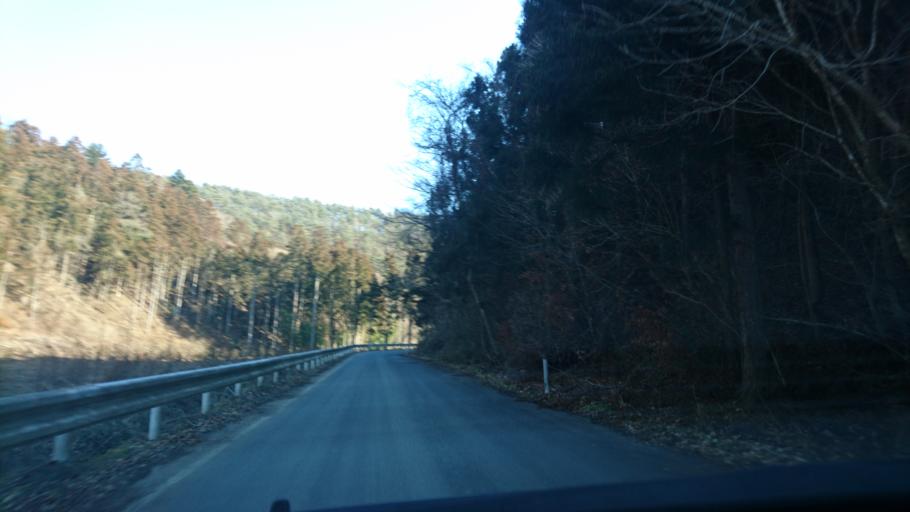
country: JP
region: Iwate
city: Ichinoseki
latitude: 38.7946
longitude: 141.2589
